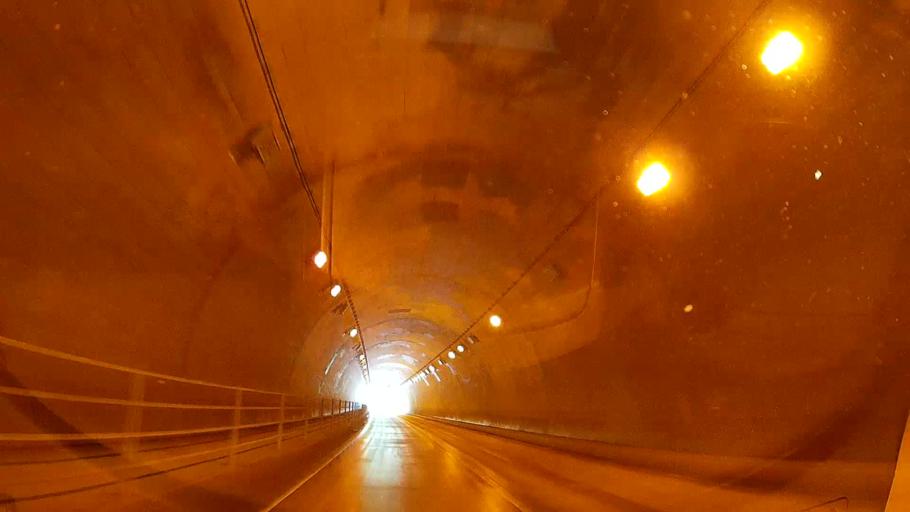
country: JP
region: Oita
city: Hita
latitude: 33.1320
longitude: 130.9904
